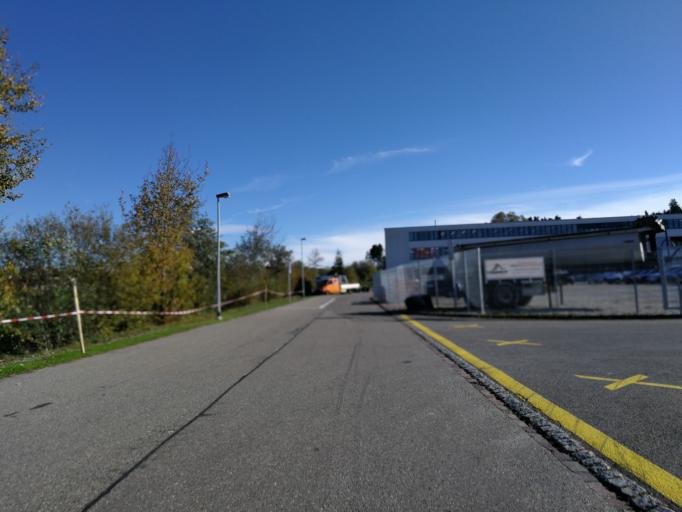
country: CH
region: Zurich
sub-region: Bezirk Meilen
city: Oetwil am See
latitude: 47.2749
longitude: 8.7271
